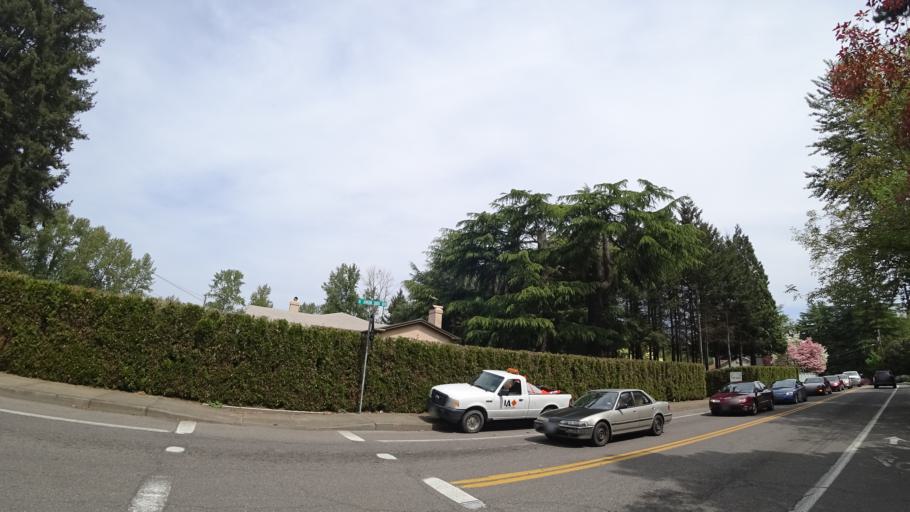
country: US
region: Oregon
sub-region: Clackamas County
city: Milwaukie
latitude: 45.4603
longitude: -122.6201
